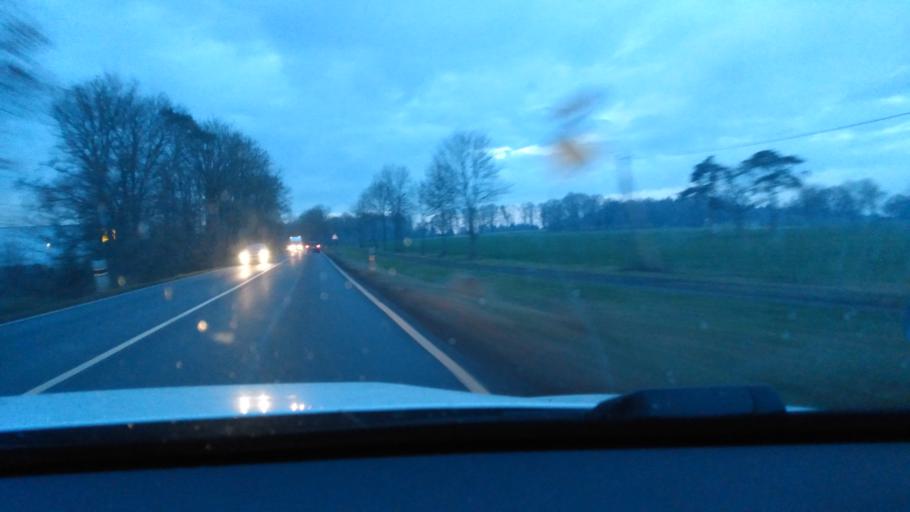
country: DE
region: Rheinland-Pfalz
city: Kircheib
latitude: 50.7132
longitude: 7.4144
